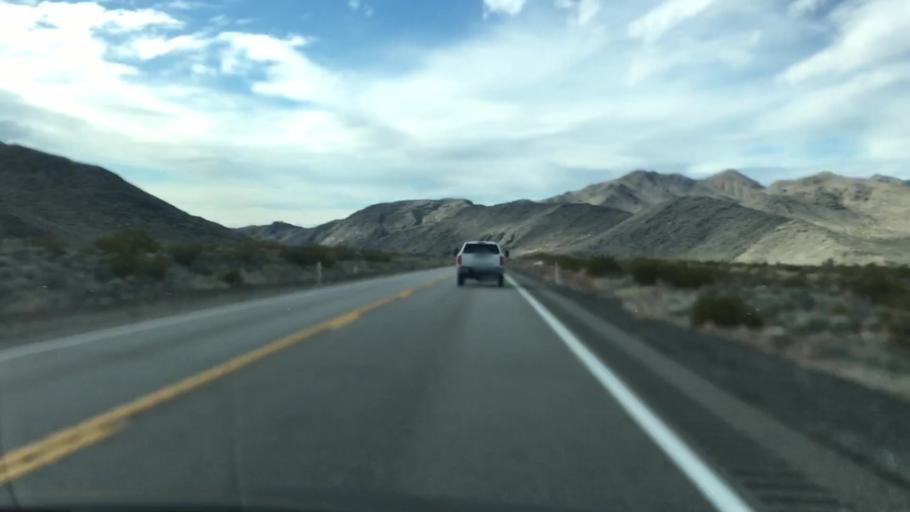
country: US
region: Nevada
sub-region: Nye County
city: Pahrump
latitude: 36.5890
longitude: -116.0461
